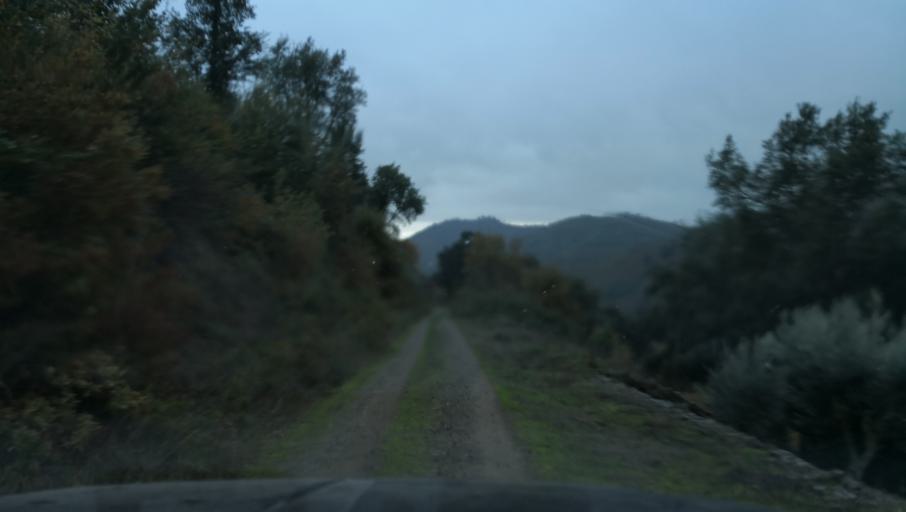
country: PT
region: Vila Real
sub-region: Santa Marta de Penaguiao
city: Santa Marta de Penaguiao
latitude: 41.2077
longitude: -7.7596
